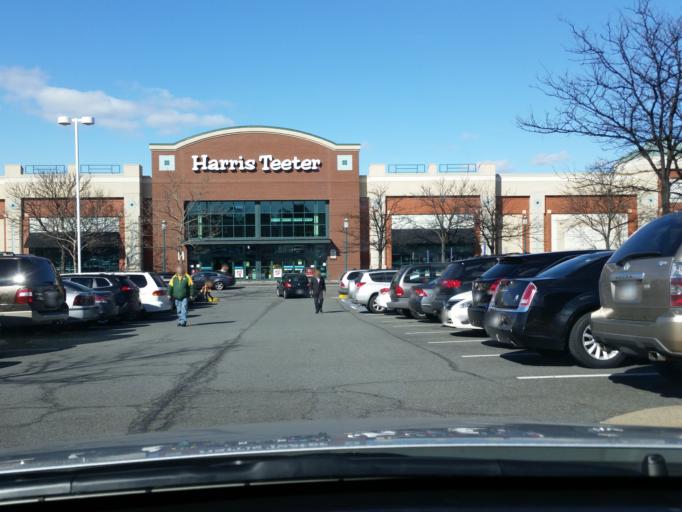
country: US
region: Virginia
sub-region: Fairfax County
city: Reston
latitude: 38.9652
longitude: -77.3549
